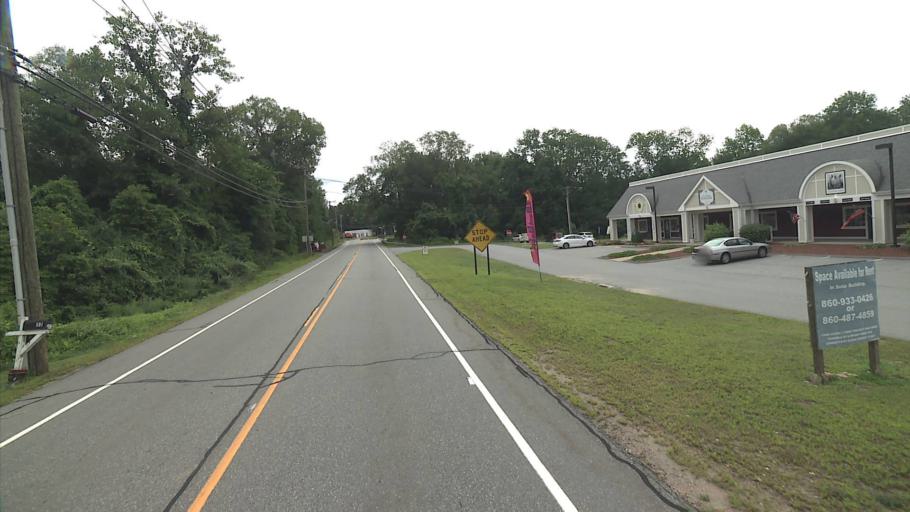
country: US
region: Connecticut
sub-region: Tolland County
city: Storrs
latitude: 41.8580
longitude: -72.1803
